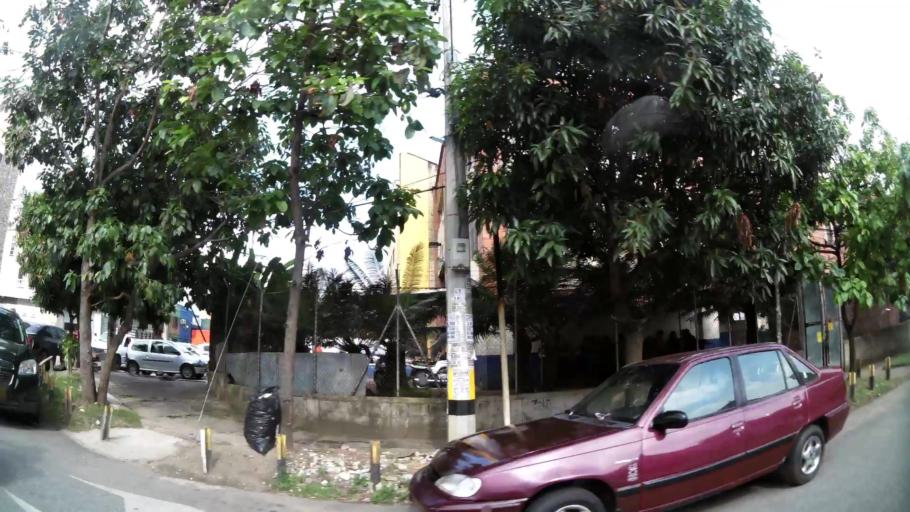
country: CO
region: Antioquia
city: Medellin
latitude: 6.2294
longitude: -75.5819
